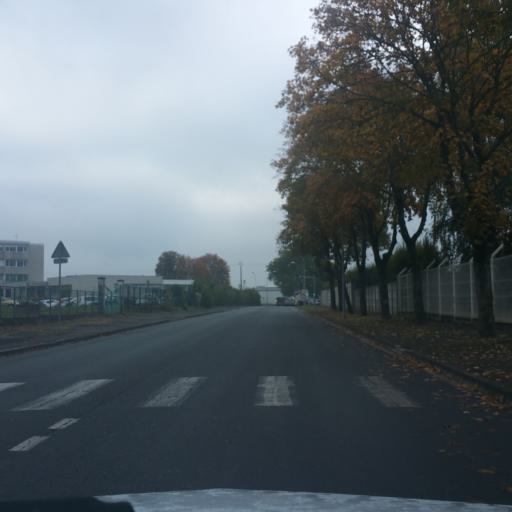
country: FR
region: Picardie
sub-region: Departement de l'Aisne
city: Laon
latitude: 49.5759
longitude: 3.6459
